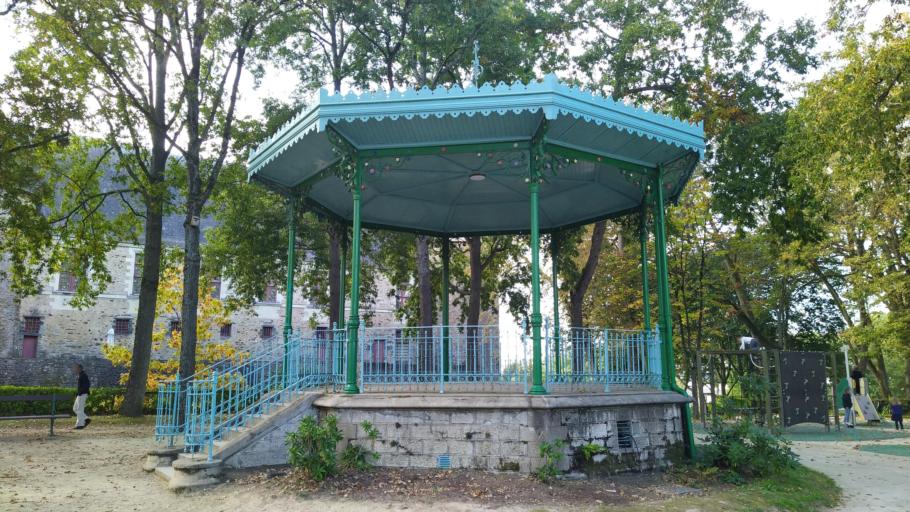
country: FR
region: Pays de la Loire
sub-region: Departement de la Loire-Atlantique
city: Chateaubriant
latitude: 47.7194
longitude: -1.3712
